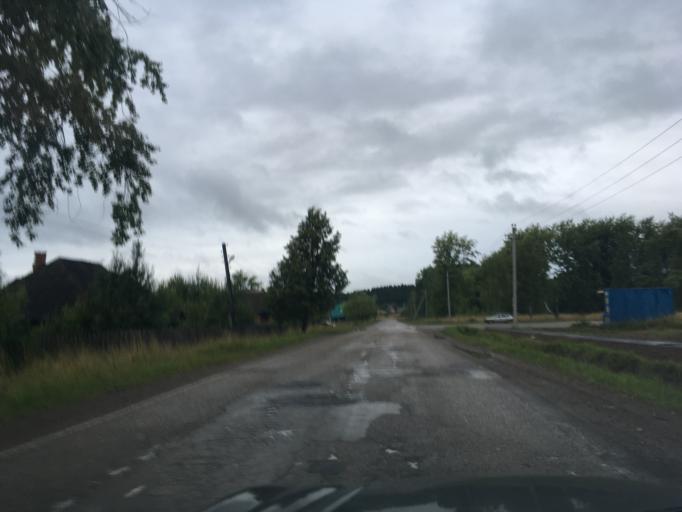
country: RU
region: Perm
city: Verkhnechusovskiye Gorodki
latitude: 58.1721
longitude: 57.1096
